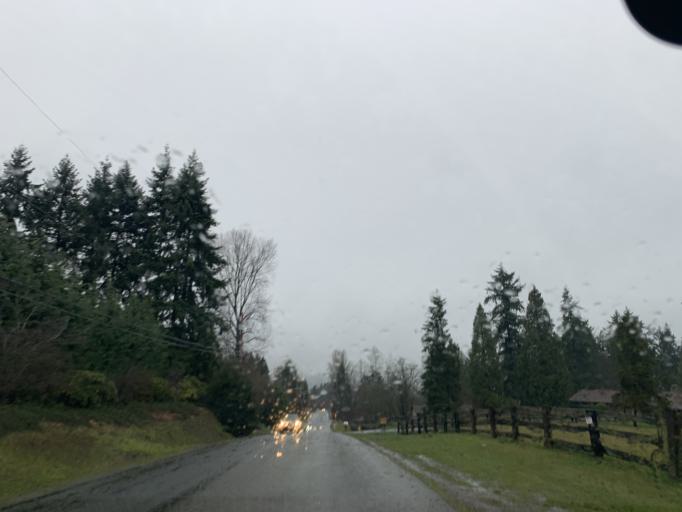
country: US
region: Washington
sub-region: King County
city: Kingsgate
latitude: 47.7343
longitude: -122.1637
